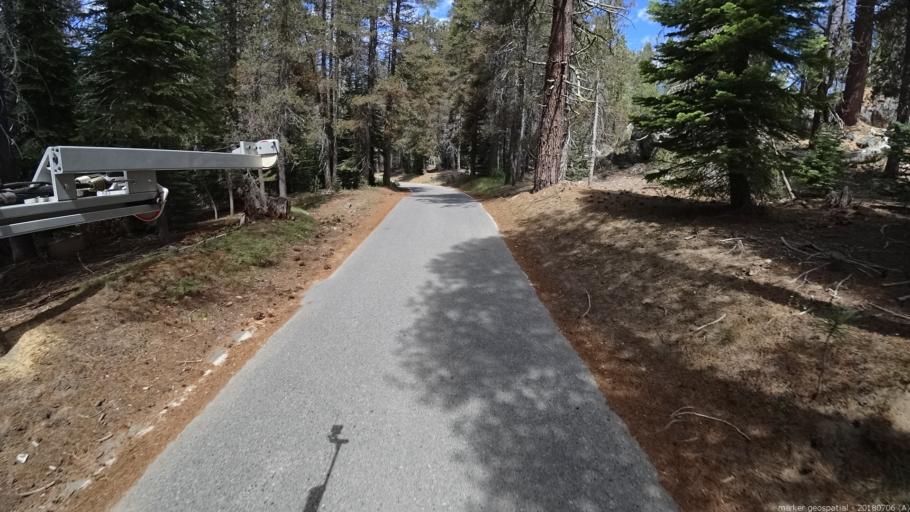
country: US
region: California
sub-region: Madera County
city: Oakhurst
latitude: 37.4472
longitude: -119.4507
